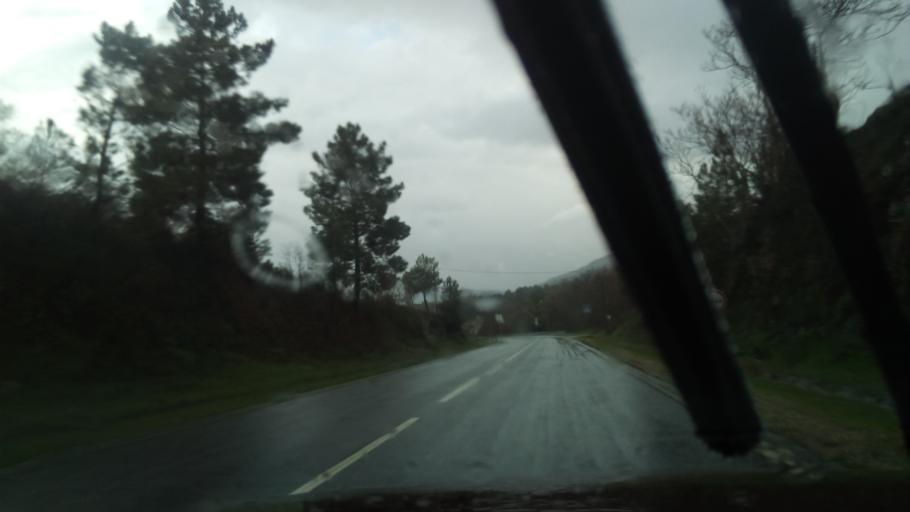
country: PT
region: Guarda
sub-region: Guarda
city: Guarda
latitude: 40.5918
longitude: -7.2897
